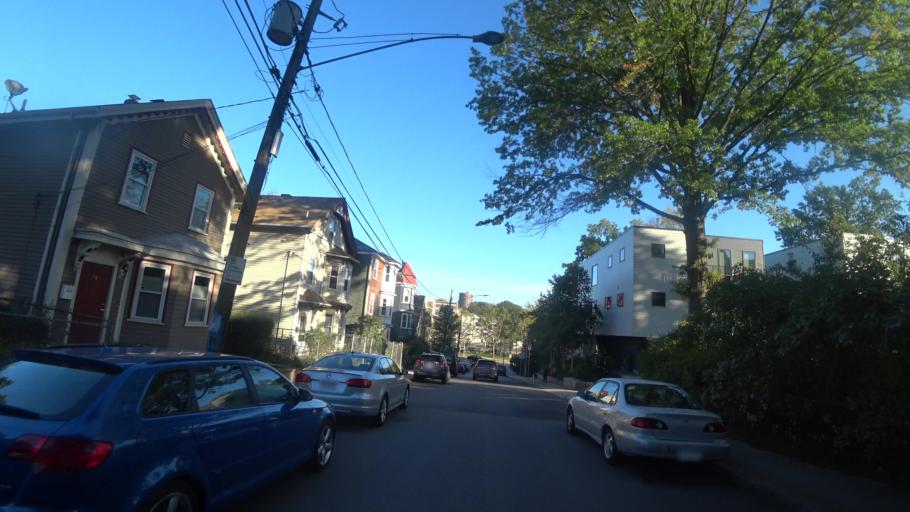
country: US
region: Massachusetts
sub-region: Suffolk County
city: Jamaica Plain
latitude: 42.3196
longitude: -71.1045
